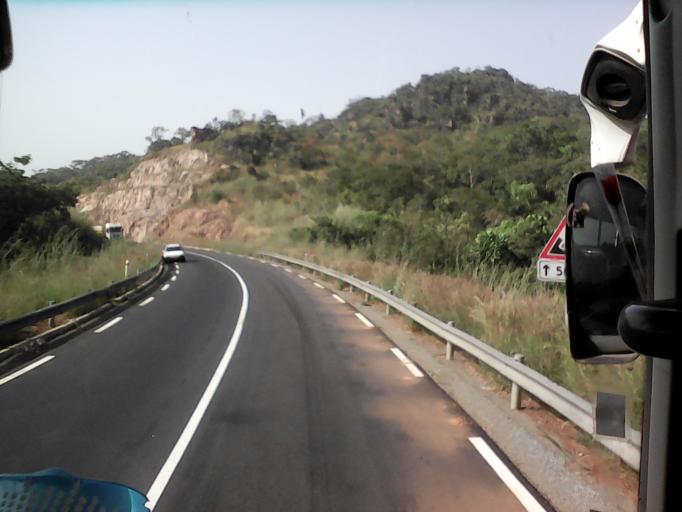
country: TG
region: Kara
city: Bafilo
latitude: 9.2664
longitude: 1.2327
